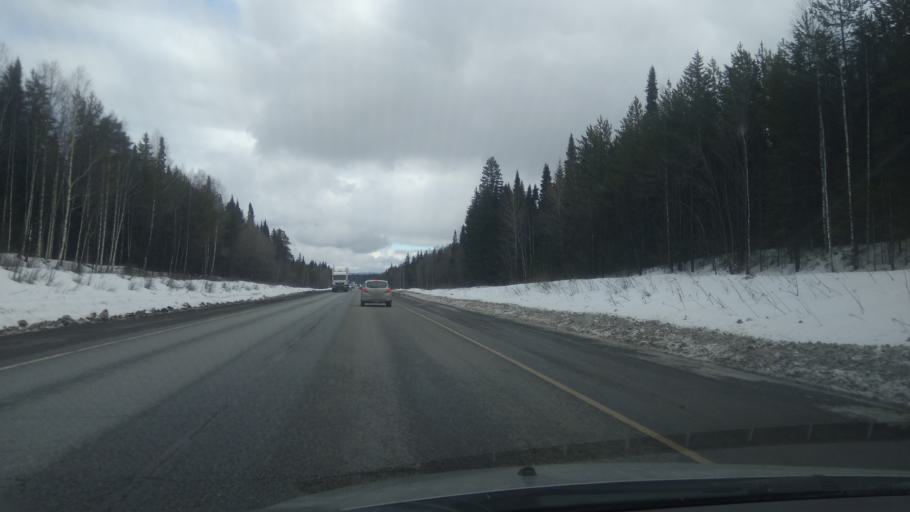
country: RU
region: Sverdlovsk
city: Druzhinino
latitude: 56.7963
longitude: 59.4223
